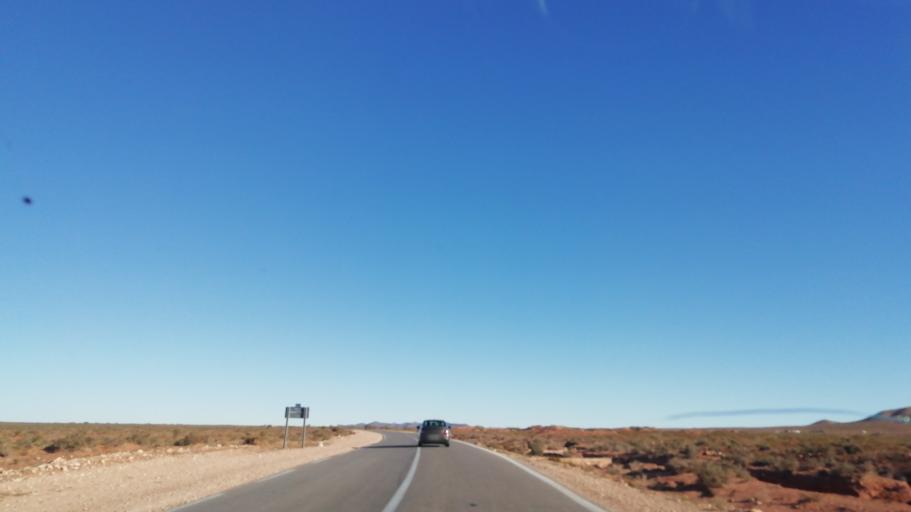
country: DZ
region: El Bayadh
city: El Abiodh Sidi Cheikh
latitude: 33.1121
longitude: 0.2529
